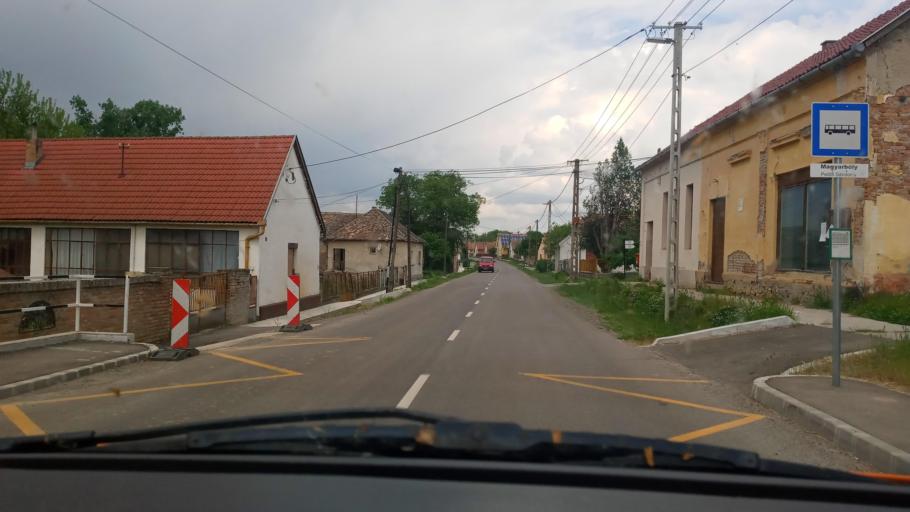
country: HU
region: Baranya
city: Villany
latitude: 45.8486
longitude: 18.4839
